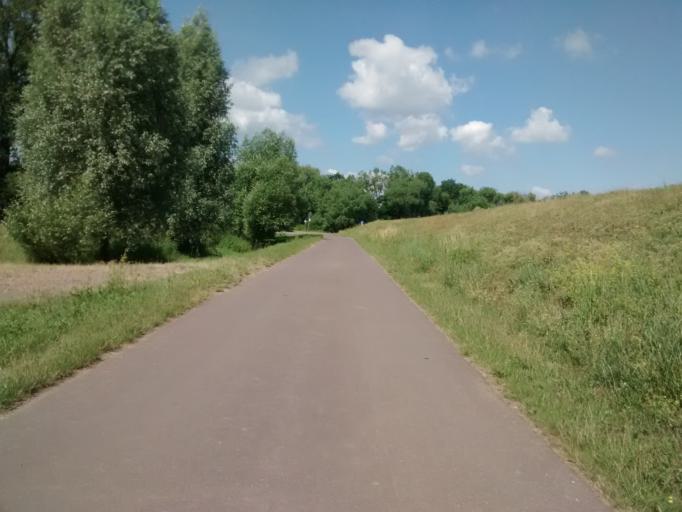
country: DE
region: Saxony-Anhalt
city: Wittenburg
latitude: 51.8471
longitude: 12.5919
